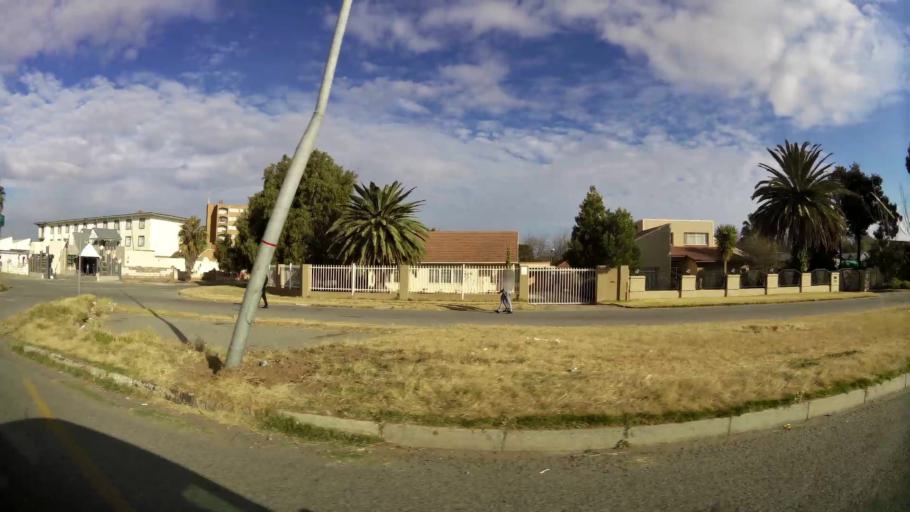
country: ZA
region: Orange Free State
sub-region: Lejweleputswa District Municipality
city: Welkom
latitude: -27.9750
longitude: 26.7088
